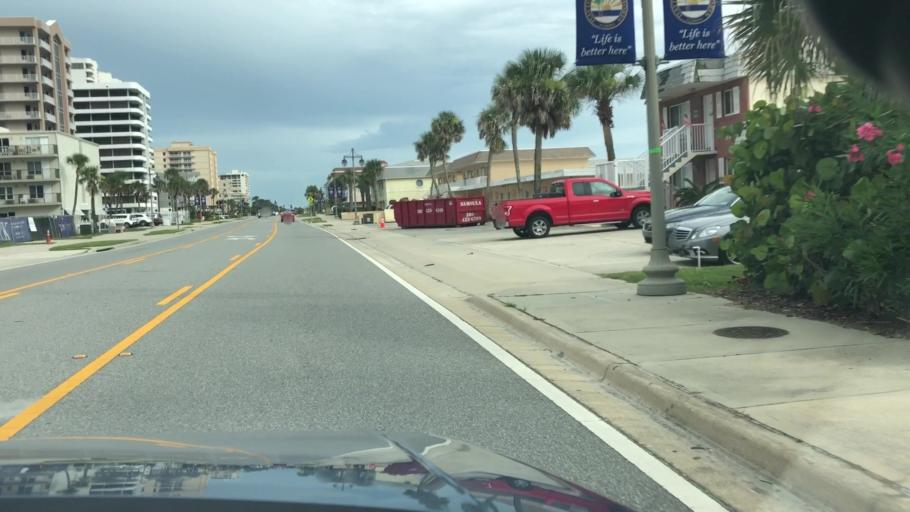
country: US
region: Florida
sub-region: Volusia County
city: Port Orange
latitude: 29.1451
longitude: -80.9660
